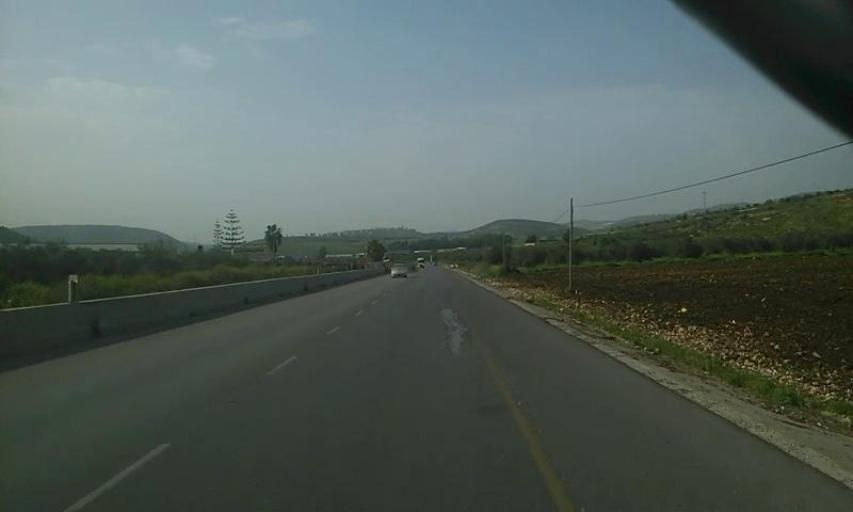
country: PS
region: West Bank
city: Dayr Sharaf
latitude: 32.2614
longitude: 35.1741
